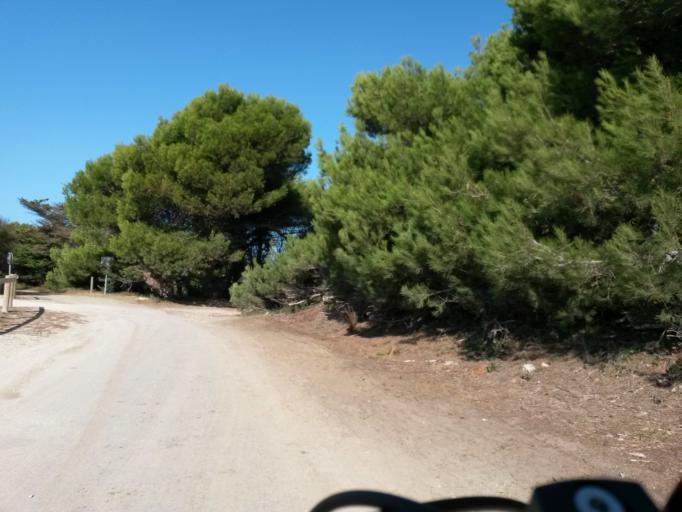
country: FR
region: Poitou-Charentes
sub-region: Departement de la Charente-Maritime
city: Le Bois-Plage-en-Re
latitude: 46.1626
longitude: -1.3621
